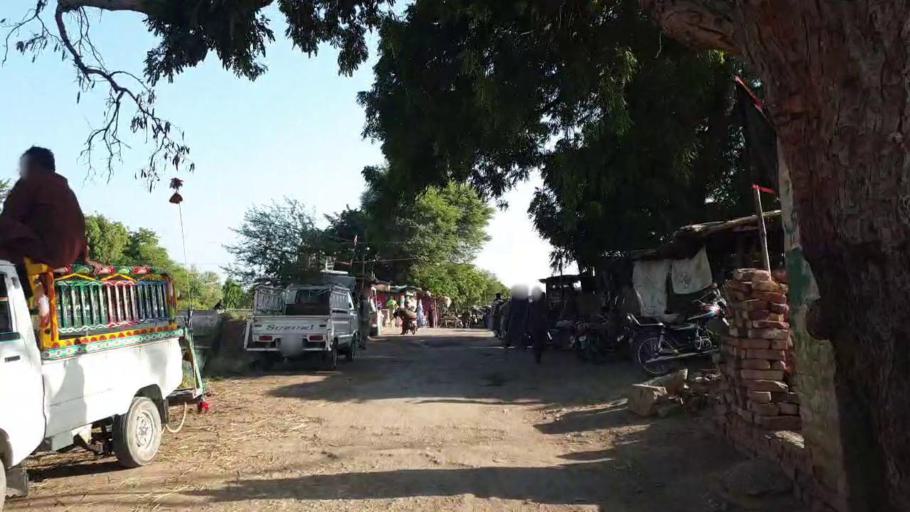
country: PK
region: Sindh
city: Hyderabad
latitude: 25.3162
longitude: 68.4295
